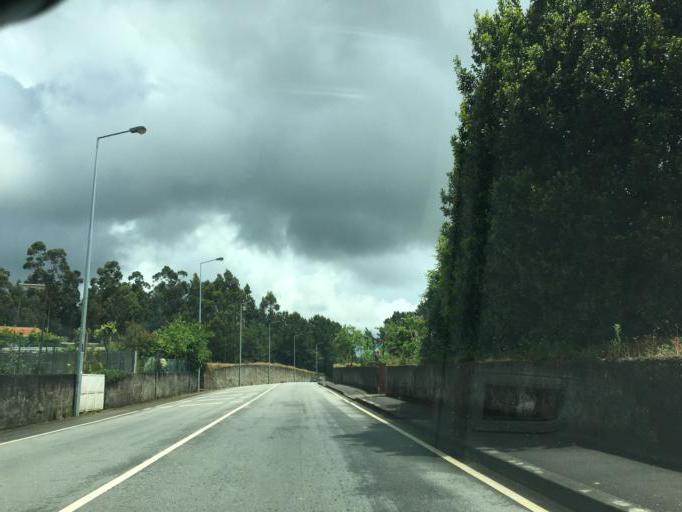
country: PT
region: Porto
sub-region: Maia
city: Nogueira
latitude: 41.2592
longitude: -8.6027
